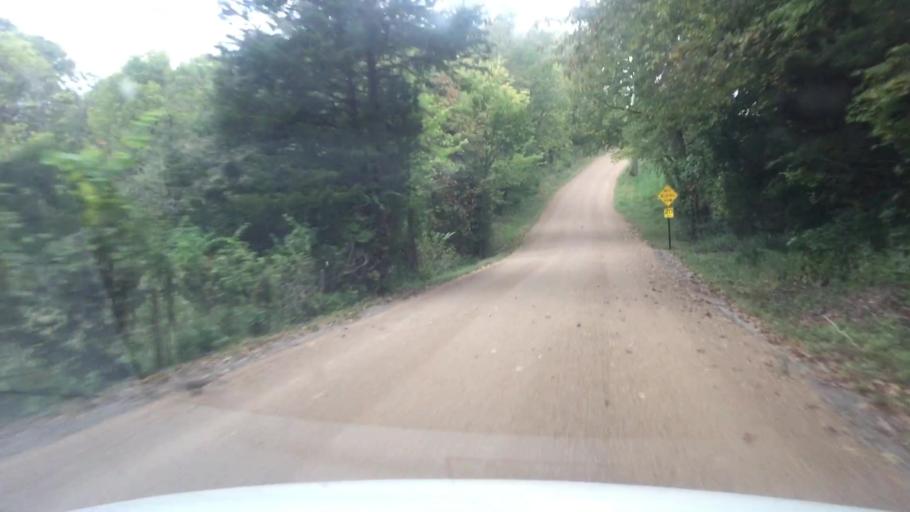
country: US
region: Missouri
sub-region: Boone County
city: Columbia
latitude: 38.8853
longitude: -92.4197
